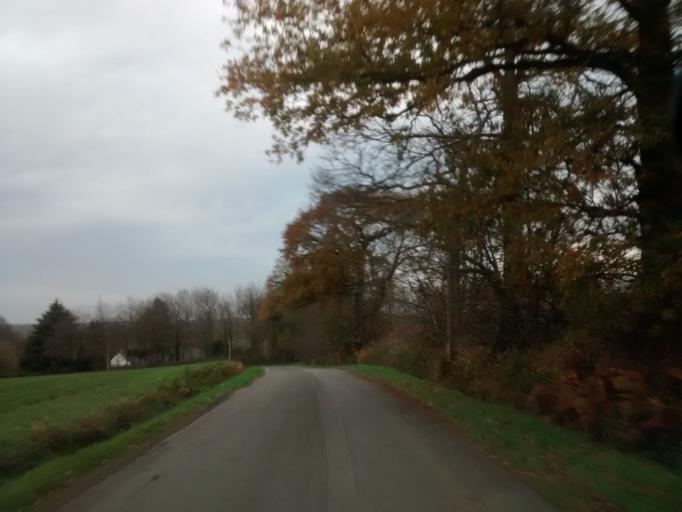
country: FR
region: Brittany
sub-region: Departement d'Ille-et-Vilaine
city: Acigne
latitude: 48.1209
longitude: -1.5617
